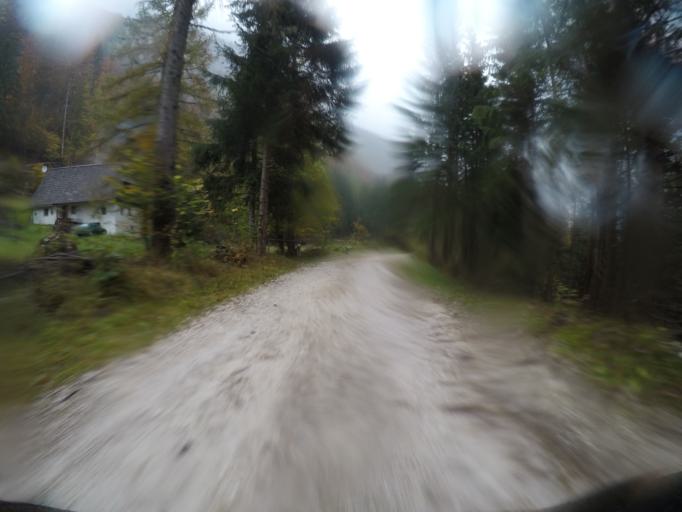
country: SI
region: Kranjska Gora
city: Kranjska Gora
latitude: 46.4064
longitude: 13.7152
